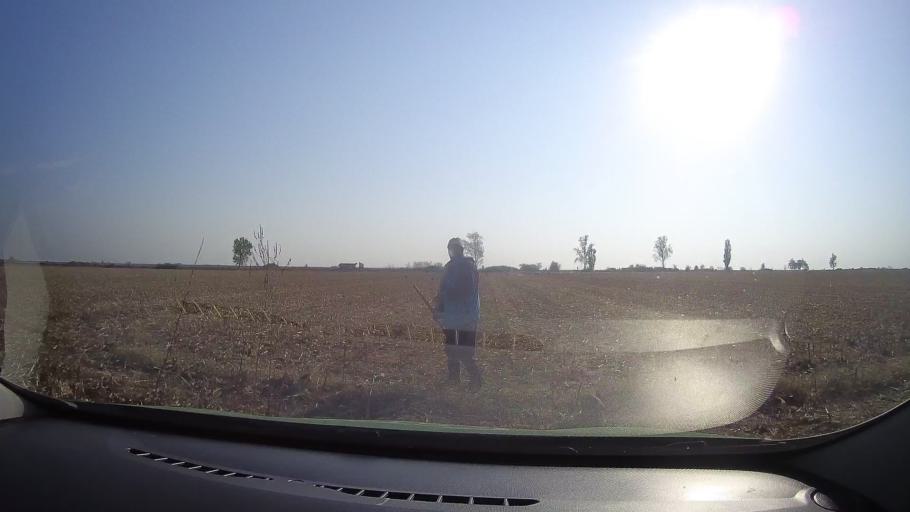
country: RO
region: Arad
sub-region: Comuna Pilu
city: Pilu
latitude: 46.5574
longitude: 21.3443
